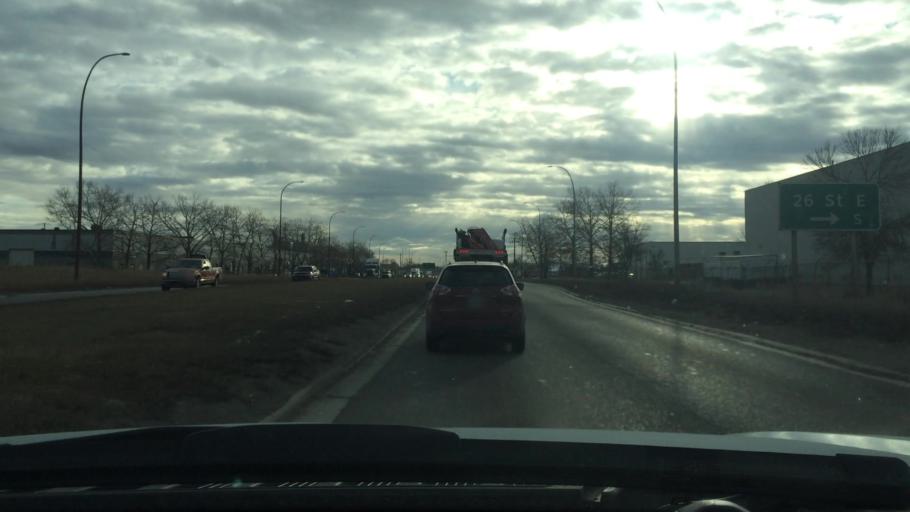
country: CA
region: Alberta
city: Calgary
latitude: 51.0065
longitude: -113.9995
